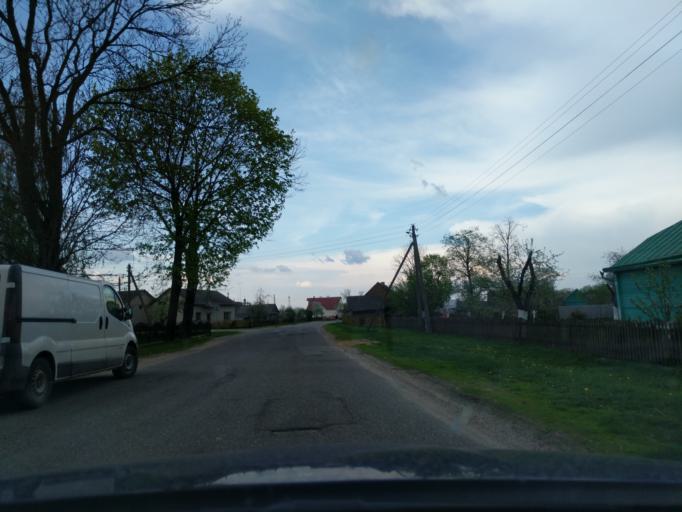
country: BY
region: Grodnenskaya
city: Lyubcha
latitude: 53.7523
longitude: 26.0518
